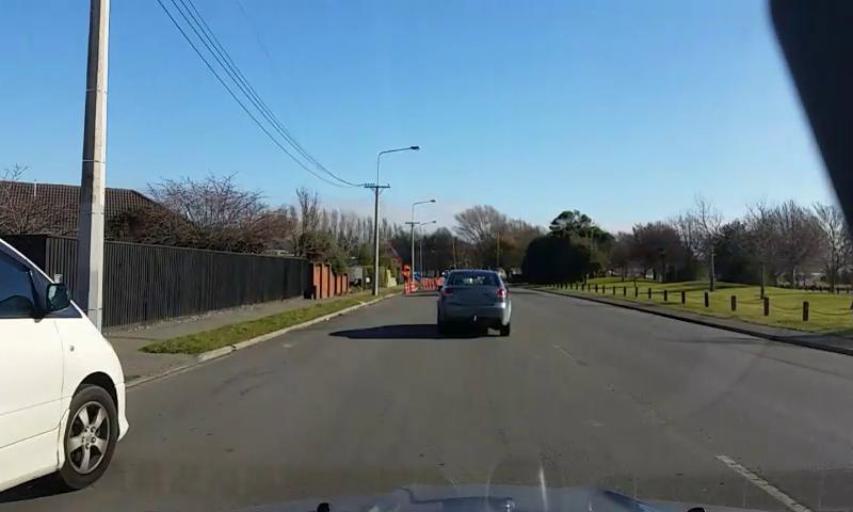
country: NZ
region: Canterbury
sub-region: Christchurch City
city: Christchurch
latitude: -43.4945
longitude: 172.7074
